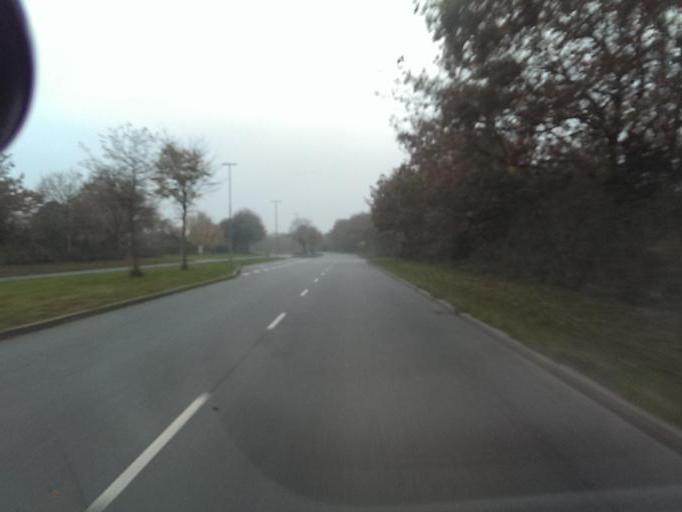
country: DK
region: South Denmark
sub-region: Esbjerg Kommune
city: Esbjerg
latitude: 55.5110
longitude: 8.4358
